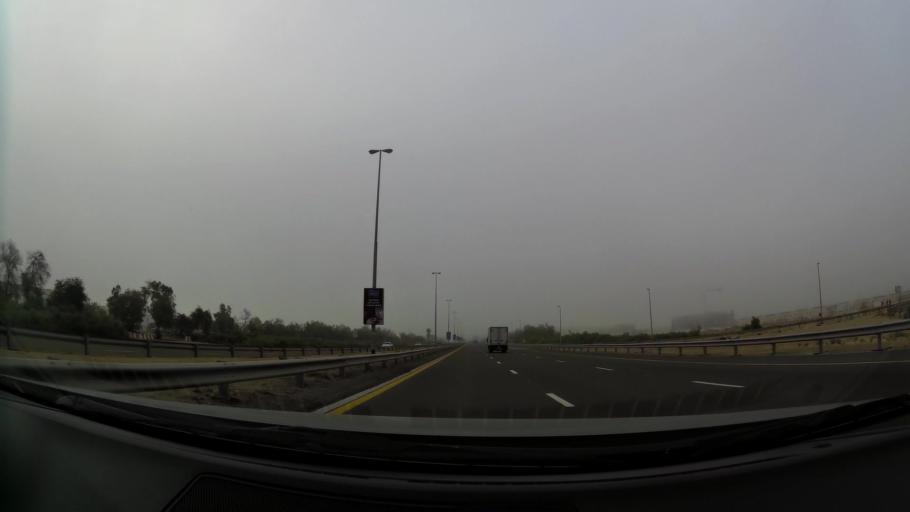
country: AE
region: Dubai
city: Dubai
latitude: 25.1309
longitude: 55.3554
